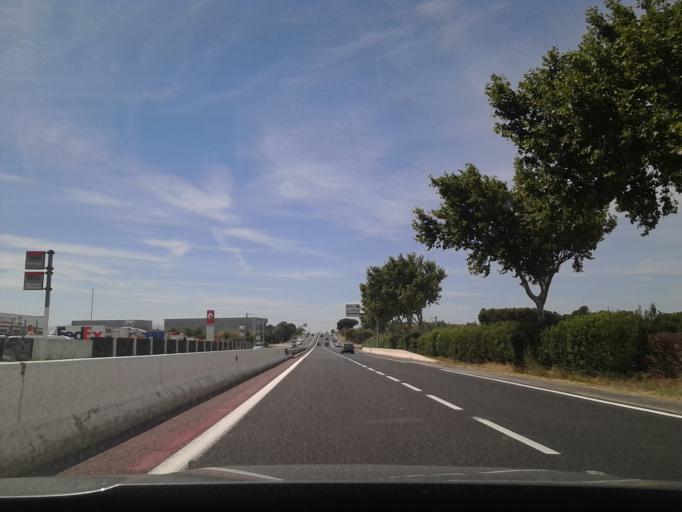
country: FR
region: Languedoc-Roussillon
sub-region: Departement des Pyrenees-Orientales
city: Pia
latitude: 42.7574
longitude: 2.8967
